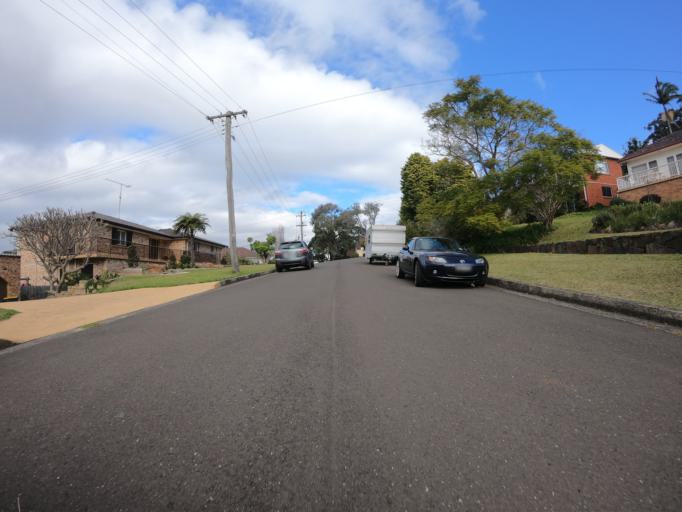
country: AU
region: New South Wales
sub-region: Wollongong
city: Mount Ousley
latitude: -34.3969
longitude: 150.8782
